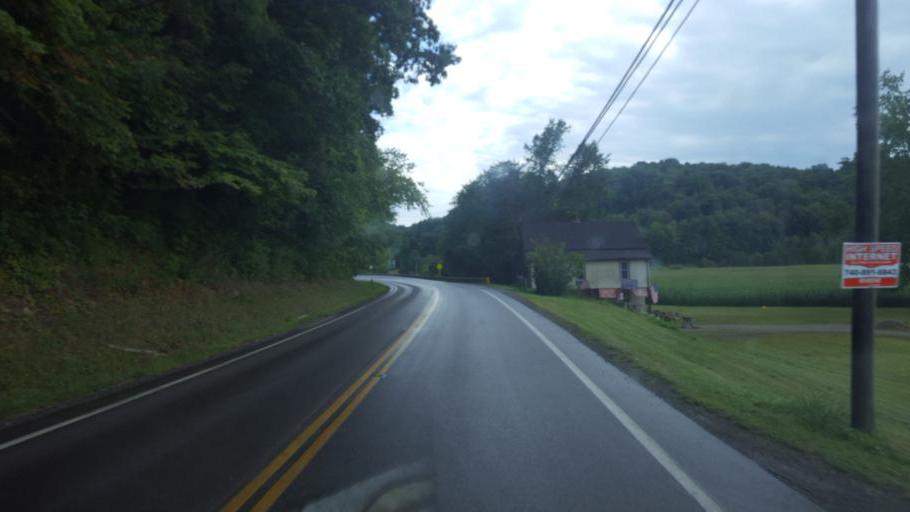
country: US
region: Ohio
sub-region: Holmes County
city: Millersburg
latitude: 40.5156
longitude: -81.9228
